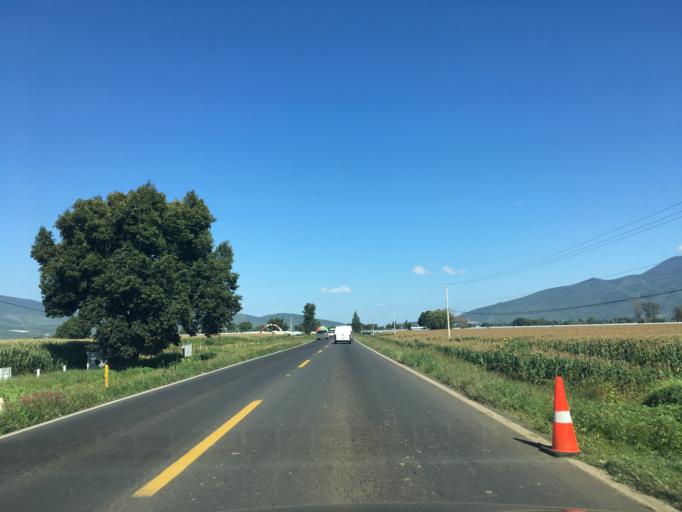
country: MX
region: Mexico
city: Tangancicuaro de Arista
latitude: 19.8637
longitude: -102.1891
